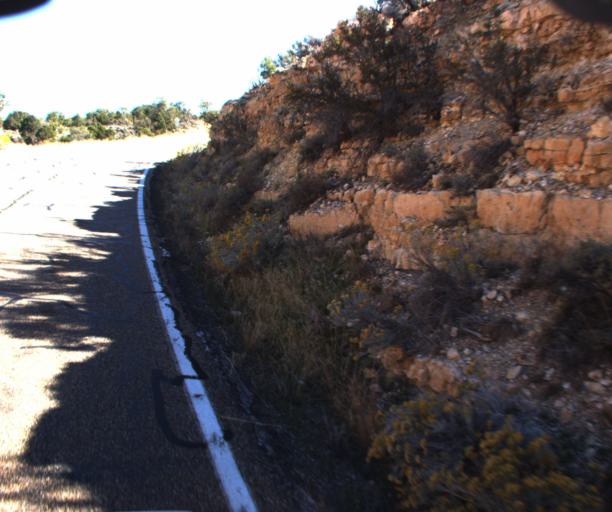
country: US
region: Arizona
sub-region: Coconino County
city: Fredonia
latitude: 36.8481
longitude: -112.2587
